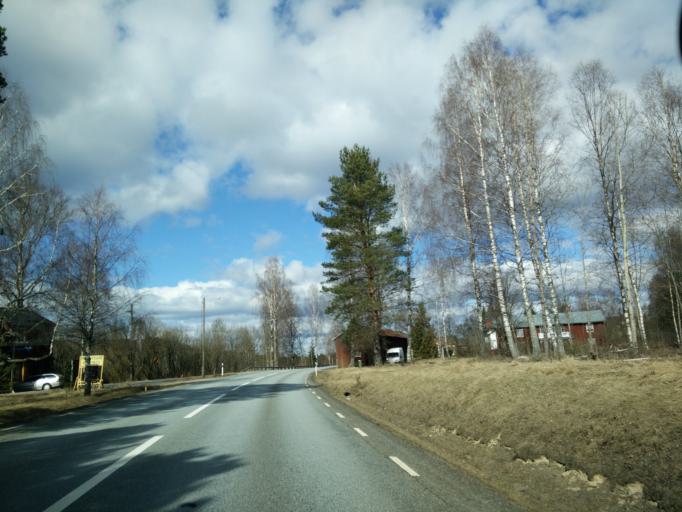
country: SE
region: Vaermland
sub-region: Munkfors Kommun
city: Munkfors
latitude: 59.9010
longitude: 13.5588
